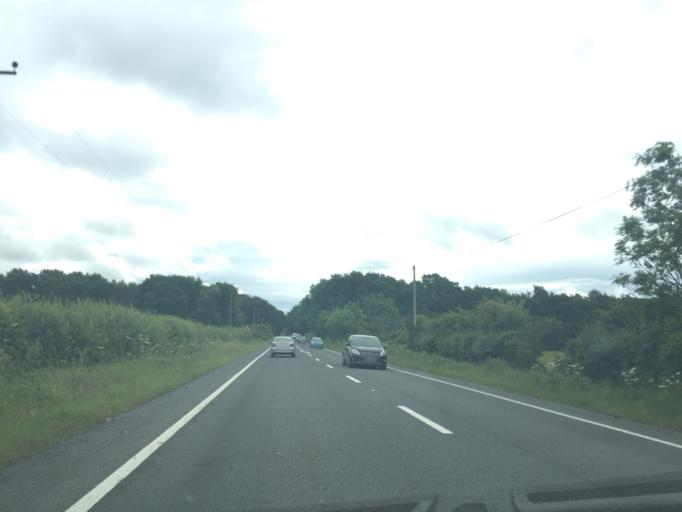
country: GB
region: England
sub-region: Dorset
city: Wareham
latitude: 50.6542
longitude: -2.0834
